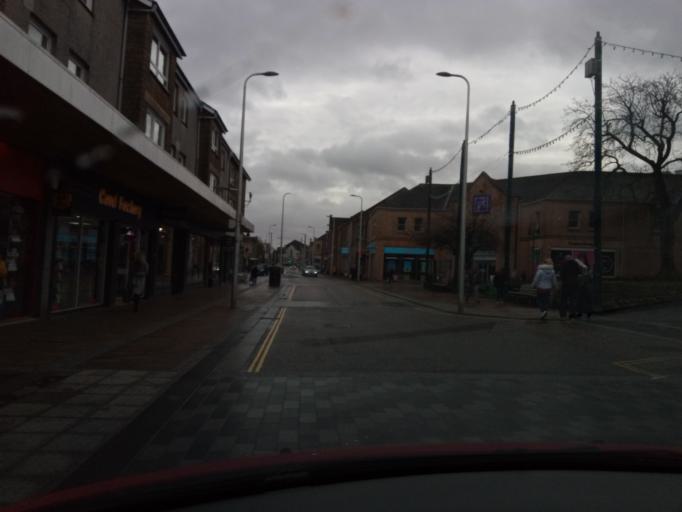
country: GB
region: Scotland
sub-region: East Dunbartonshire
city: Kirkintilloch
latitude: 55.9402
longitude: -4.1578
